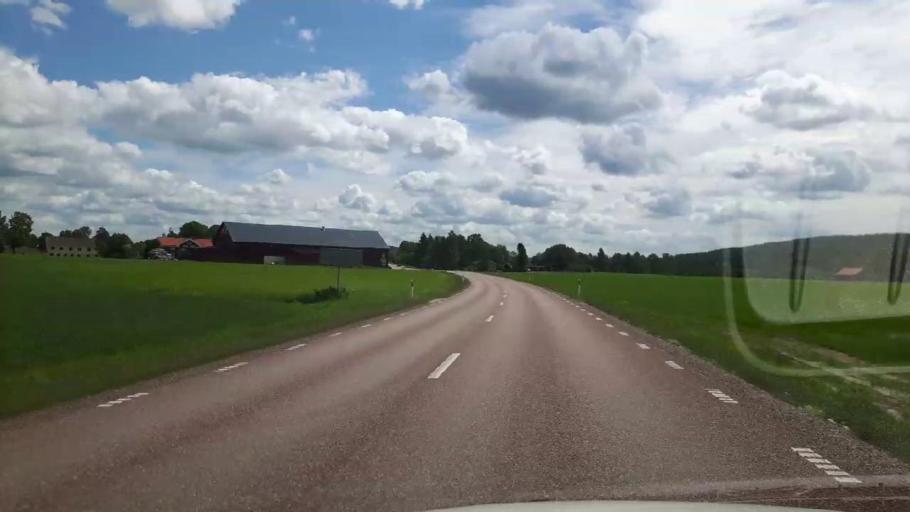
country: SE
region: Dalarna
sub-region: Saters Kommun
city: Saeter
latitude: 60.3998
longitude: 15.8771
